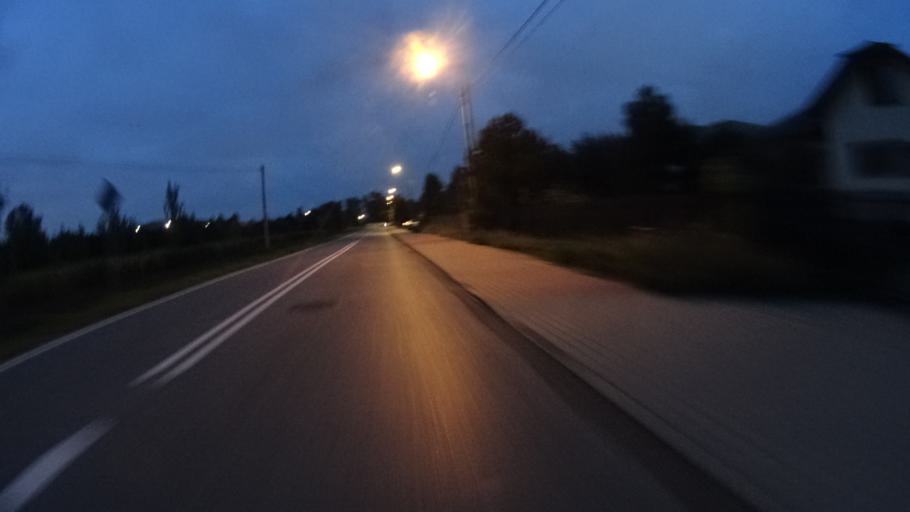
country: PL
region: Masovian Voivodeship
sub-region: Powiat warszawski zachodni
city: Babice
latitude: 52.2269
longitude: 20.8590
